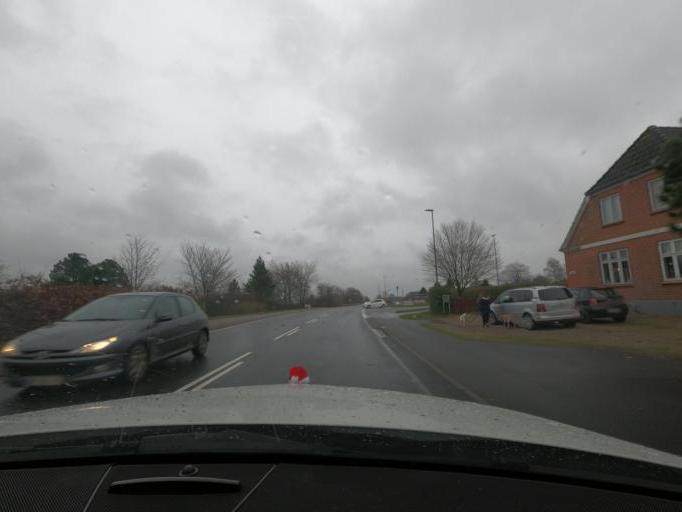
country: DK
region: South Denmark
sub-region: Haderslev Kommune
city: Starup
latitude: 55.2439
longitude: 9.5364
